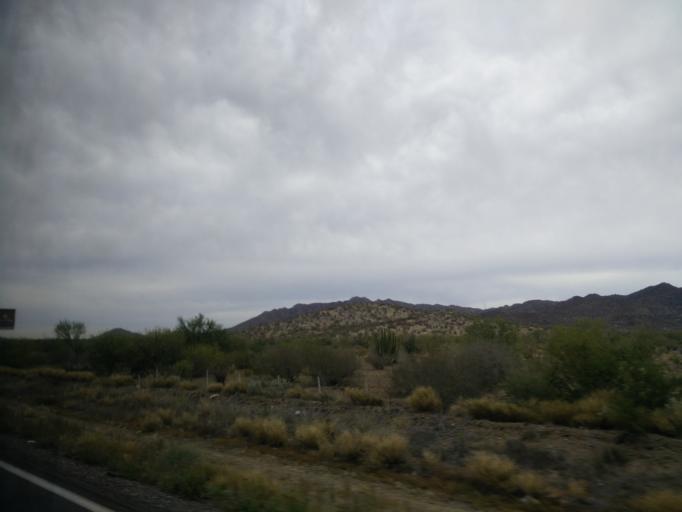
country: MX
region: Sonora
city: Hermosillo
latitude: 28.9370
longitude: -110.9566
